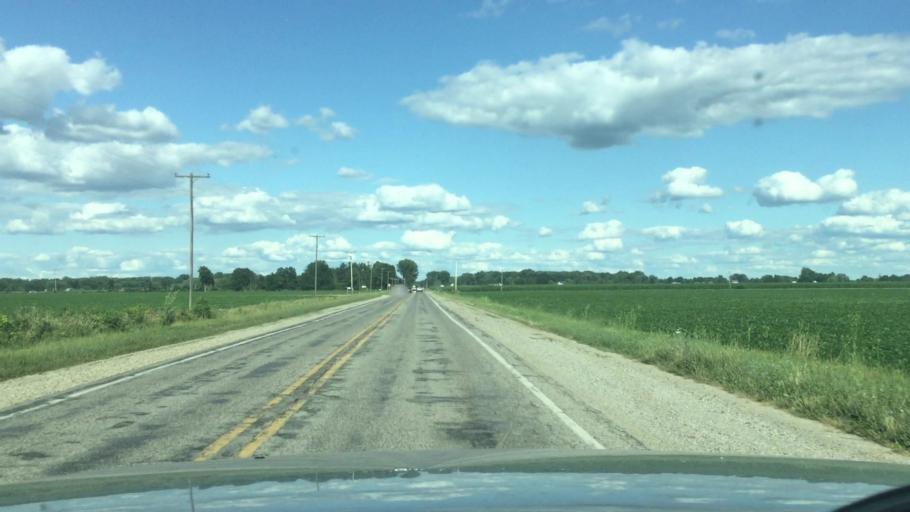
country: US
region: Michigan
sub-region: Saginaw County
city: Shields
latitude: 43.3796
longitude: -84.0912
